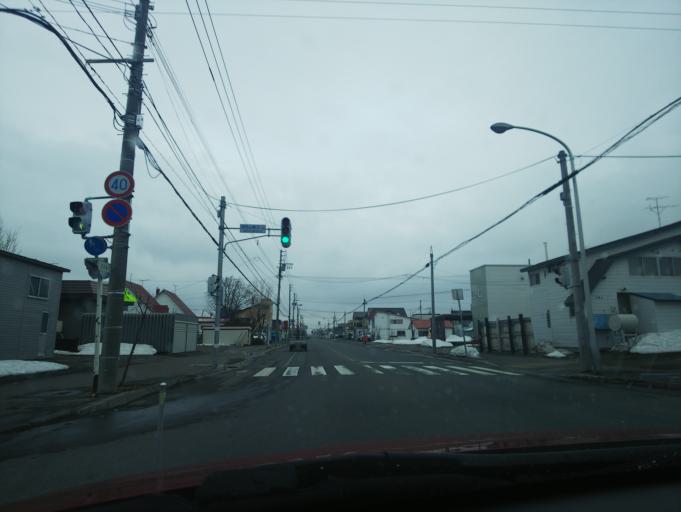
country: JP
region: Hokkaido
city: Nayoro
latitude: 44.3540
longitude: 142.4503
